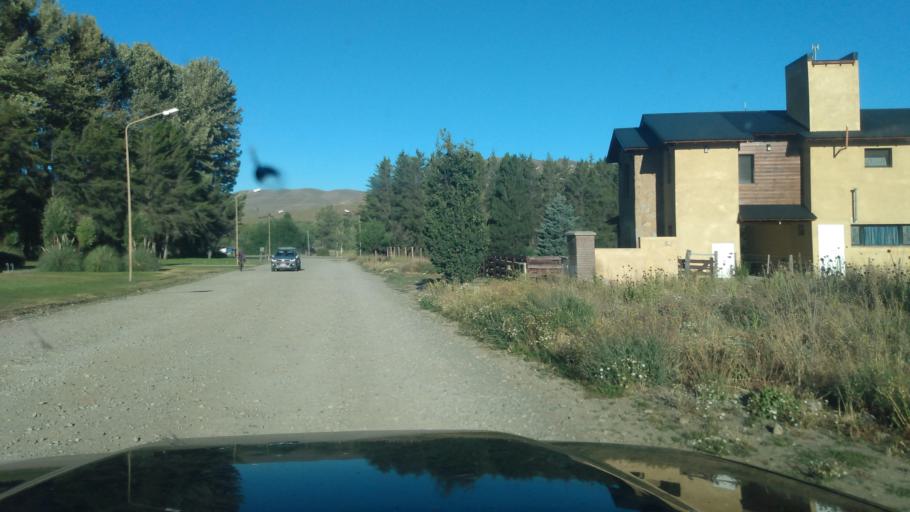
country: AR
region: Neuquen
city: Junin de los Andes
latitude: -39.9631
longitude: -71.0817
